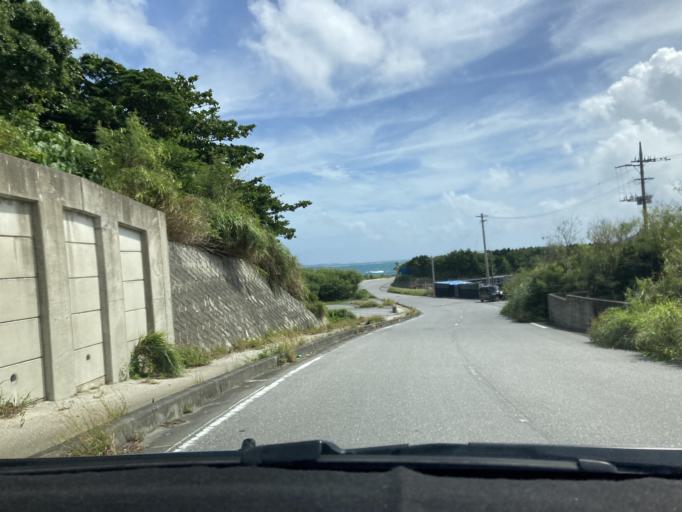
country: JP
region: Okinawa
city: Ginowan
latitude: 26.1874
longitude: 127.8208
